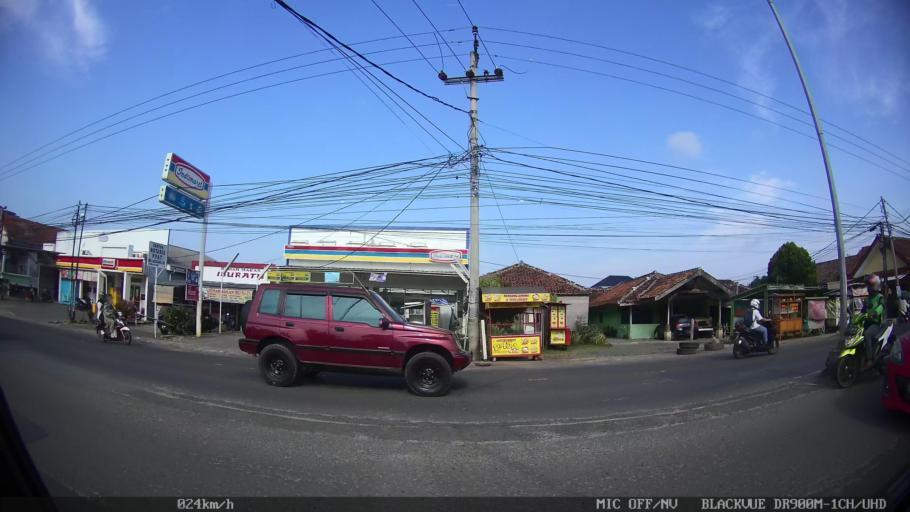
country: ID
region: Lampung
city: Kedaton
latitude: -5.3701
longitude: 105.2279
